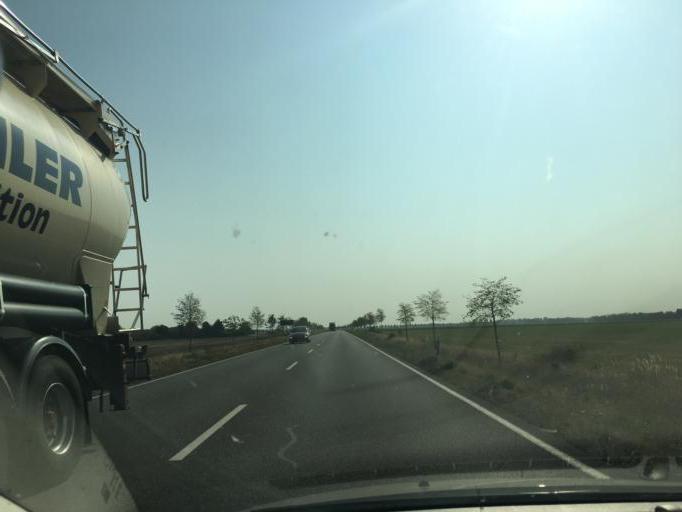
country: DE
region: Saxony-Anhalt
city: Schonebeck
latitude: 51.9910
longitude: 11.7350
